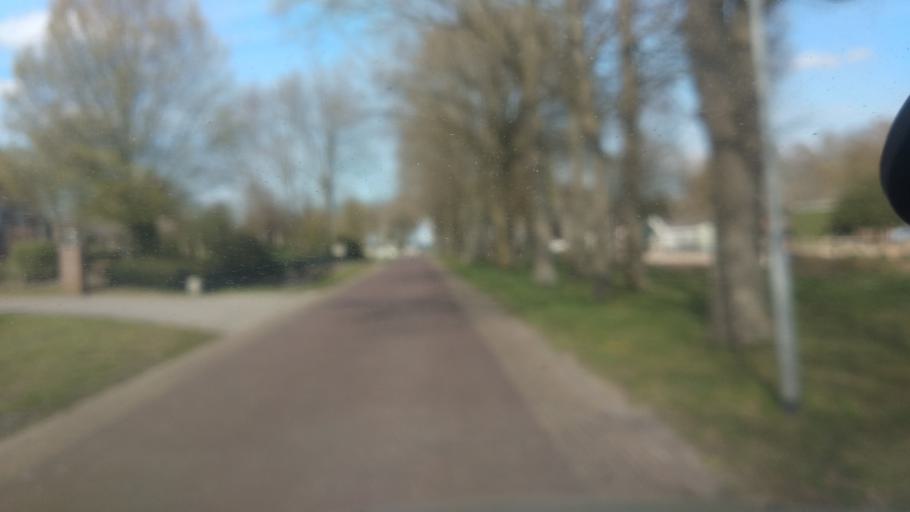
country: NL
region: Drenthe
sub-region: Gemeente Borger-Odoorn
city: Borger
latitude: 52.9494
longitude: 6.8220
